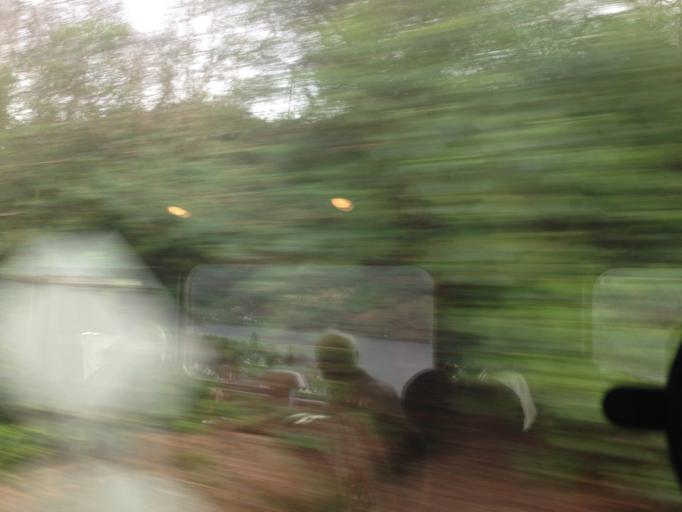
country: GB
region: Scotland
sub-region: Argyll and Bute
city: Garelochhead
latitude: 56.1923
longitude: -4.7458
